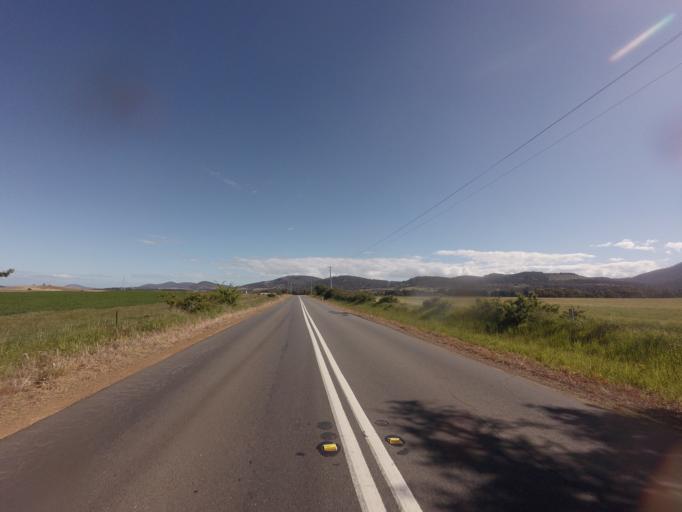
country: AU
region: Tasmania
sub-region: Clarence
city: Cambridge
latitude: -42.7589
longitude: 147.4163
